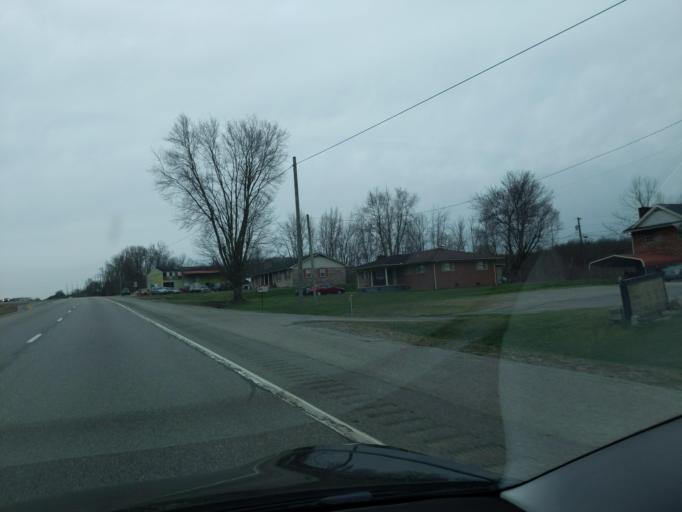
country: US
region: Kentucky
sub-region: Knox County
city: Barbourville
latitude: 36.8549
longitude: -83.7920
